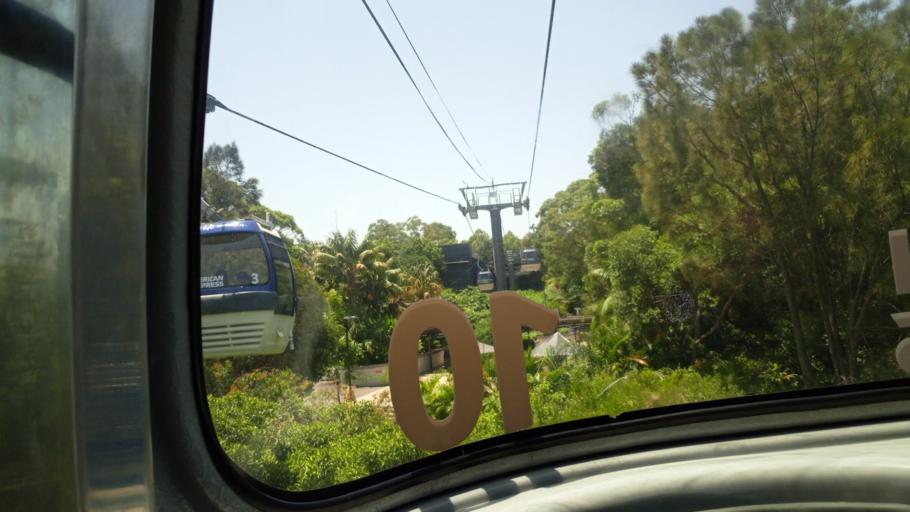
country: AU
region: New South Wales
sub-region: Mosman
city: Mosman
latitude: -33.8432
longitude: 151.2415
